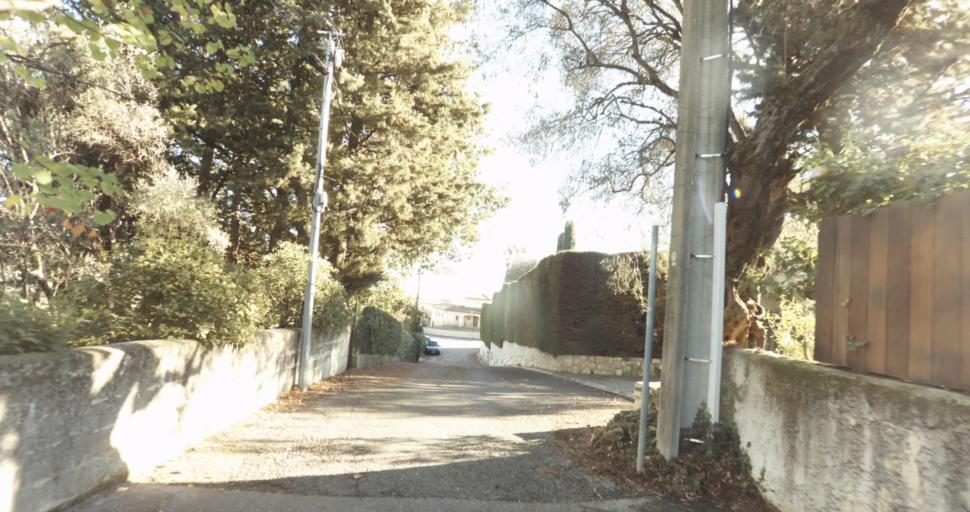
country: FR
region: Provence-Alpes-Cote d'Azur
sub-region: Departement des Alpes-Maritimes
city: La Gaude
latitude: 43.7132
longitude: 7.1364
